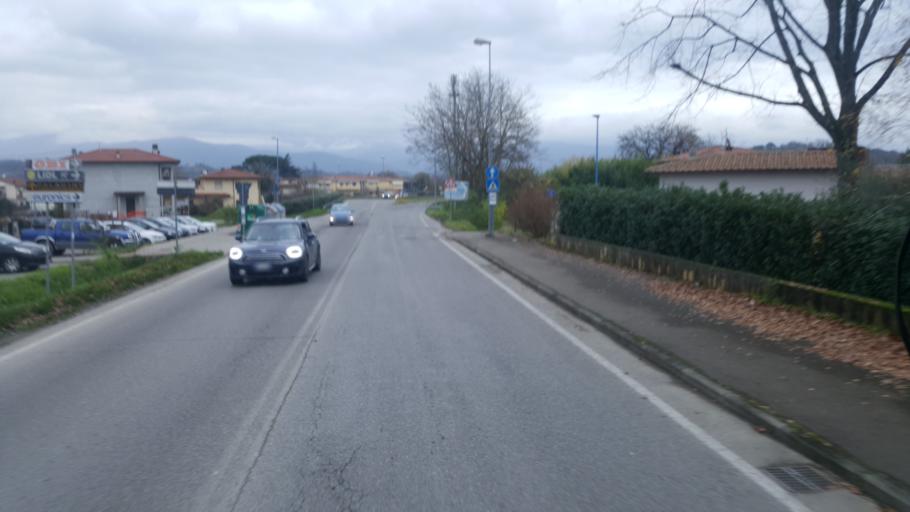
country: IT
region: Tuscany
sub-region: Province of Arezzo
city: Montevarchi
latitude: 43.5356
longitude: 11.5604
